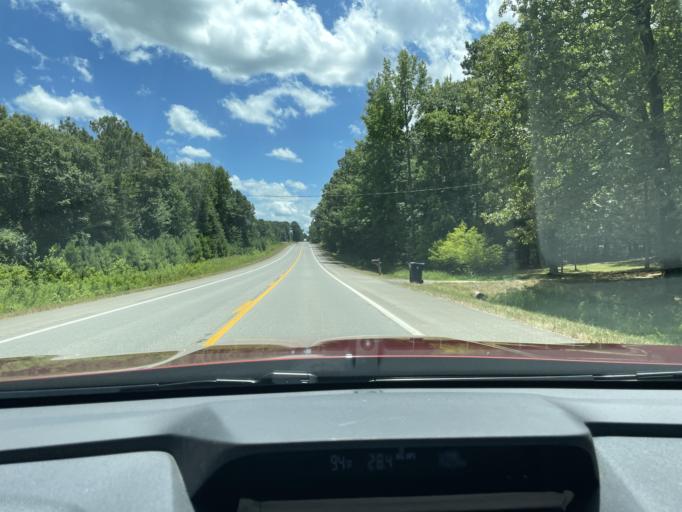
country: US
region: Arkansas
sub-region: Drew County
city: Monticello
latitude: 33.7351
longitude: -91.8170
